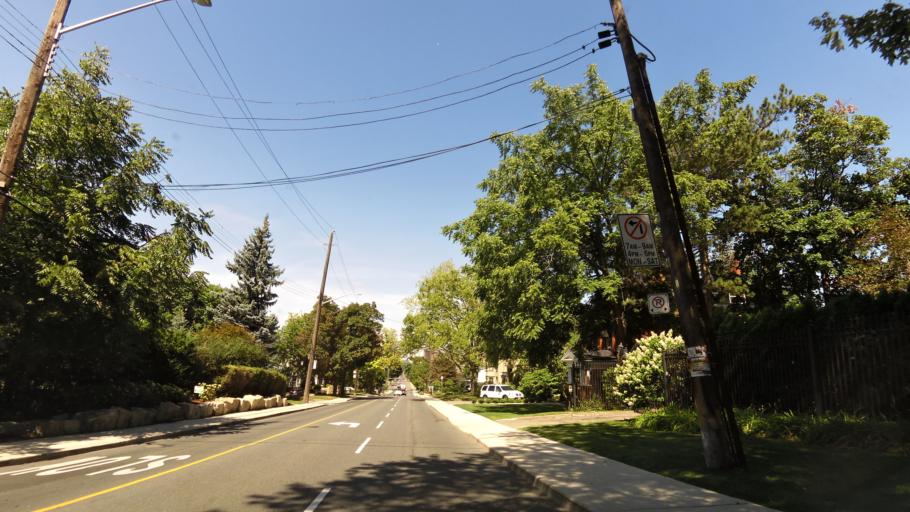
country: CA
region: Ontario
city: Hamilton
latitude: 43.2469
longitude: -79.8839
